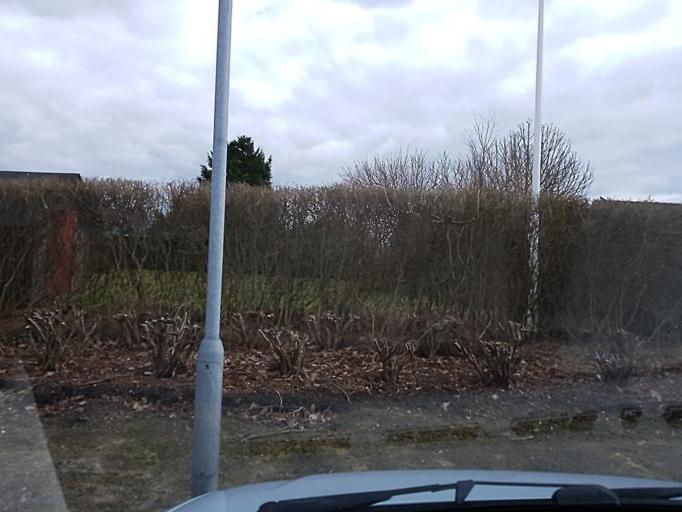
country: DK
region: South Denmark
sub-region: Esbjerg Kommune
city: Esbjerg
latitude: 55.5217
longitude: 8.4235
